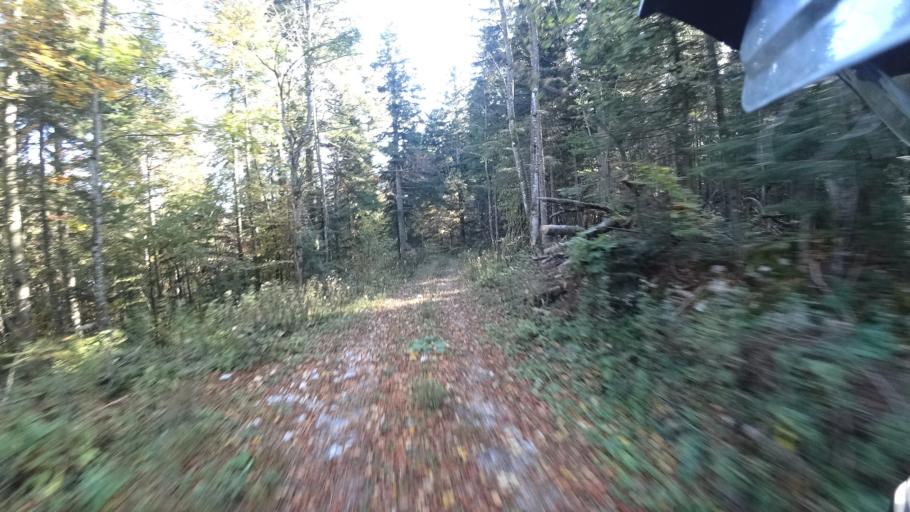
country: HR
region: Karlovacka
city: Plaski
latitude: 45.0357
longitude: 15.3477
